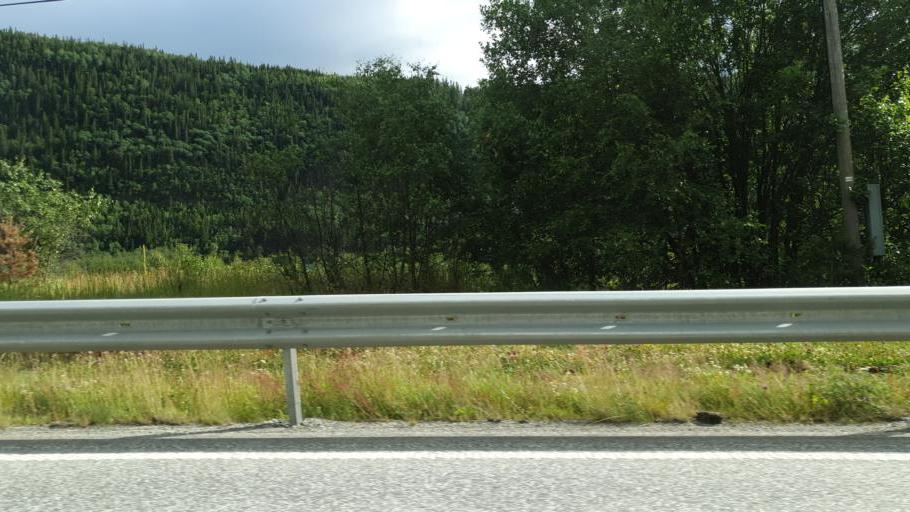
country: NO
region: Oppland
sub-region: Vaga
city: Vagamo
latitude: 61.8748
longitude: 9.1583
